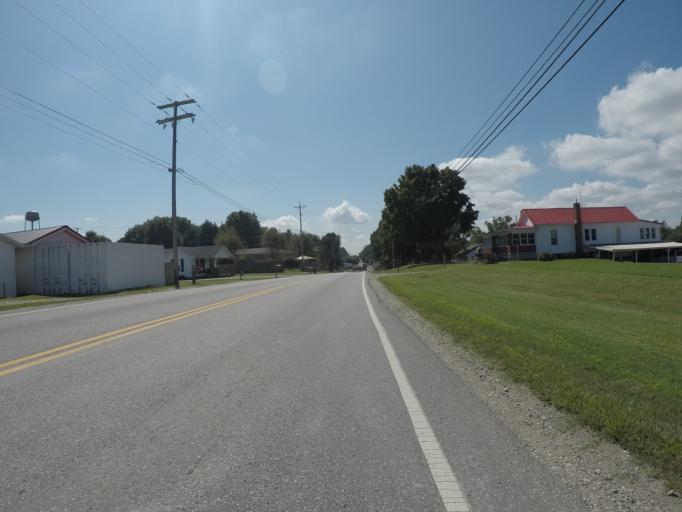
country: US
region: Ohio
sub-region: Lawrence County
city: South Point
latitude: 38.4505
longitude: -82.5938
